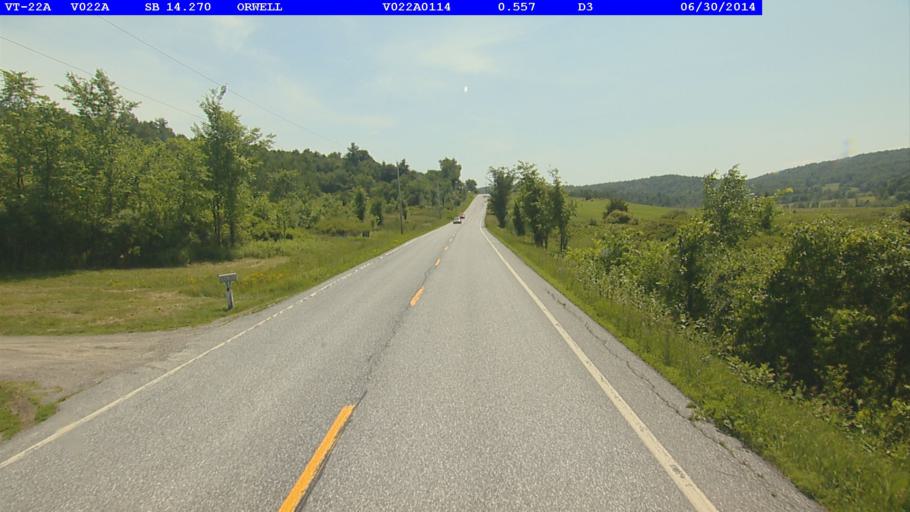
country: US
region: New York
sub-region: Essex County
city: Ticonderoga
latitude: 43.7652
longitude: -73.3107
